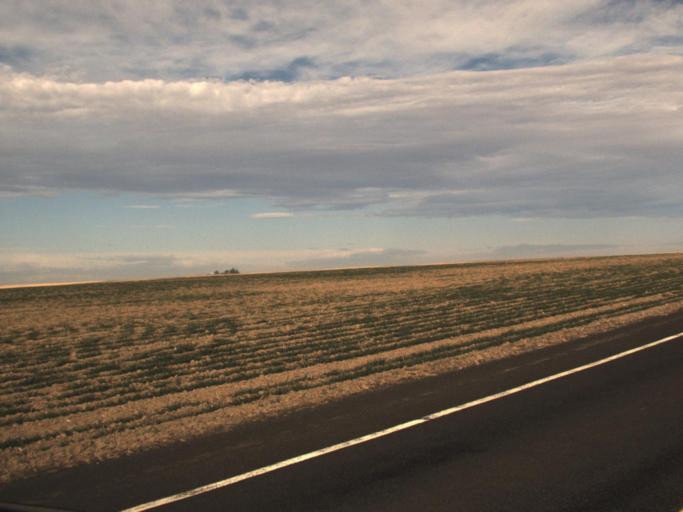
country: US
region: Washington
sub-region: Adams County
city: Ritzville
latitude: 47.1613
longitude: -118.6869
